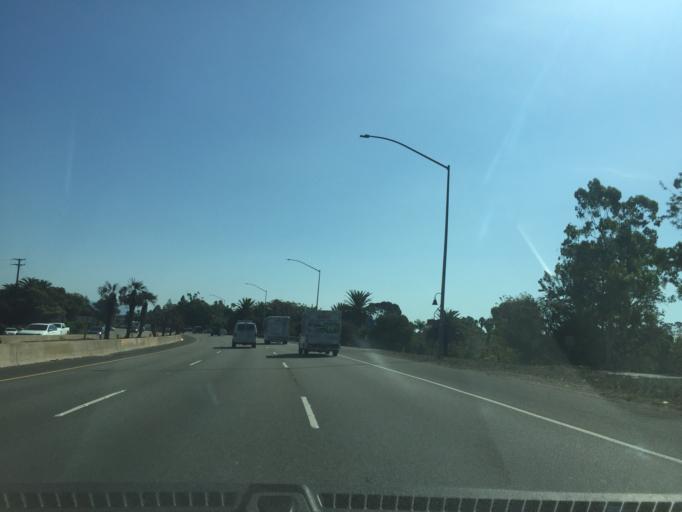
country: US
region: California
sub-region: Santa Barbara County
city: Santa Barbara
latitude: 34.4124
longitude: -119.7017
